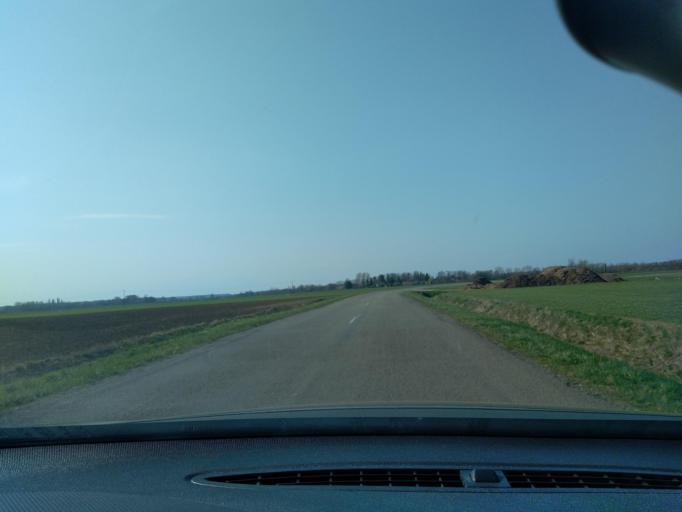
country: FR
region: Franche-Comte
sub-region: Departement du Jura
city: Mont-sous-Vaudrey
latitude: 46.9989
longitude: 5.6014
